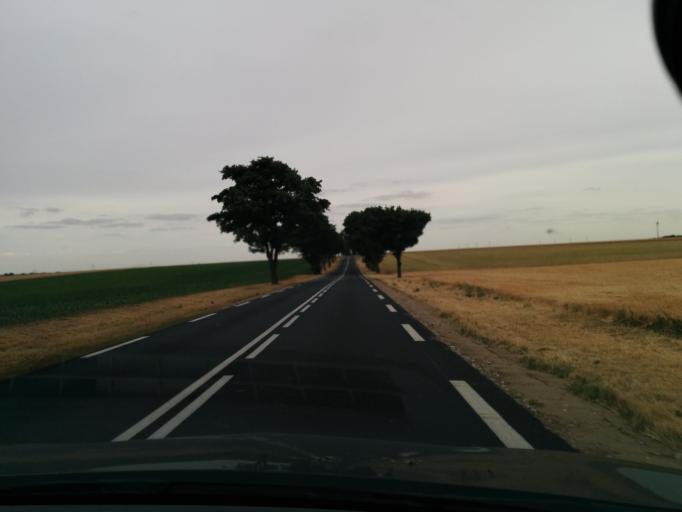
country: FR
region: Ile-de-France
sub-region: Departement de l'Essonne
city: Pussay
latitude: 48.3949
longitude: 1.9724
